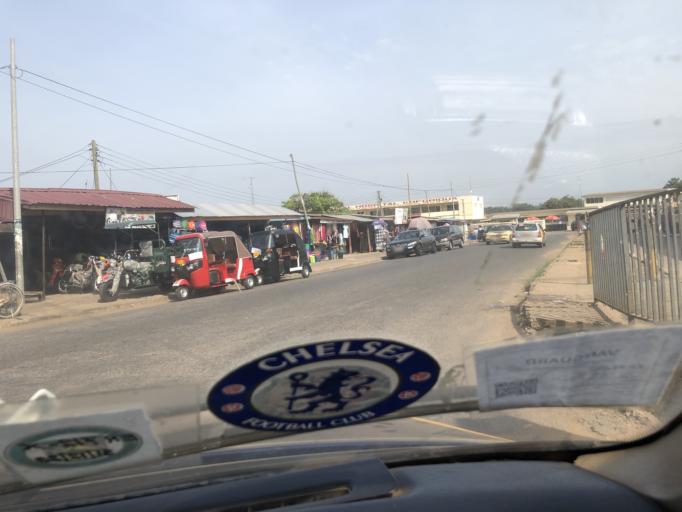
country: GH
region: Eastern
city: Koforidua
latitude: 6.0962
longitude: -0.2564
